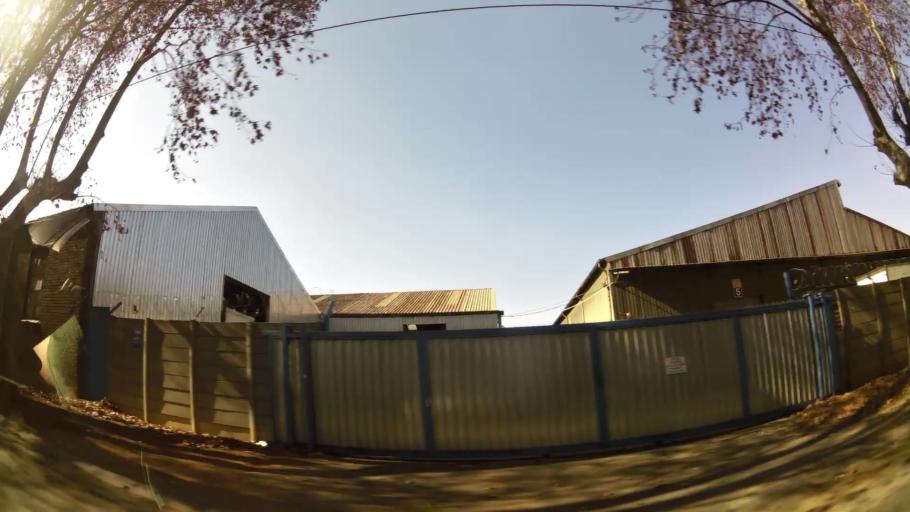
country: ZA
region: Gauteng
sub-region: City of Johannesburg Metropolitan Municipality
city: Johannesburg
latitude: -26.2021
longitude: 27.9783
